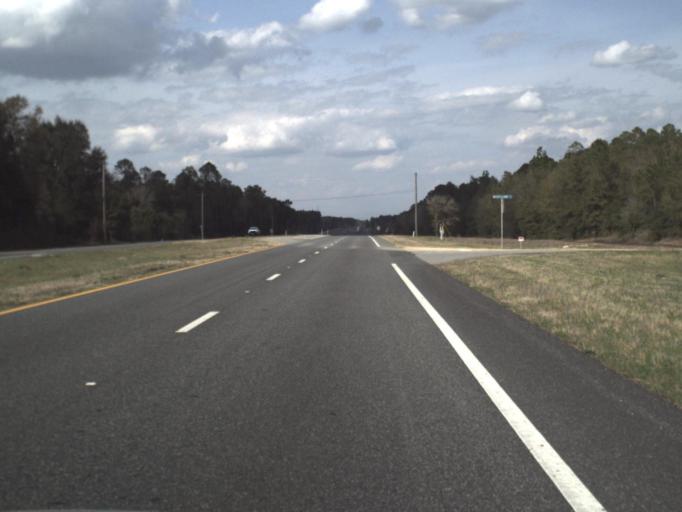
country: US
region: Florida
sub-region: Bay County
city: Youngstown
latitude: 30.4412
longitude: -85.4264
